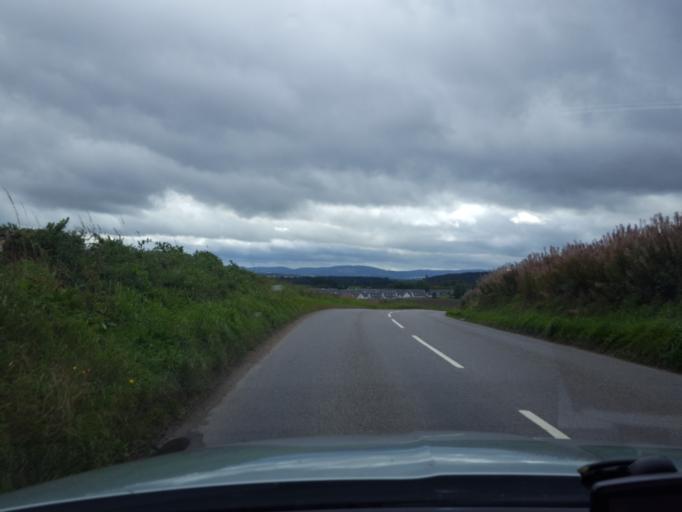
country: GB
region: Scotland
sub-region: Aberdeenshire
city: Kemnay
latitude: 57.1492
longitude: -2.4351
